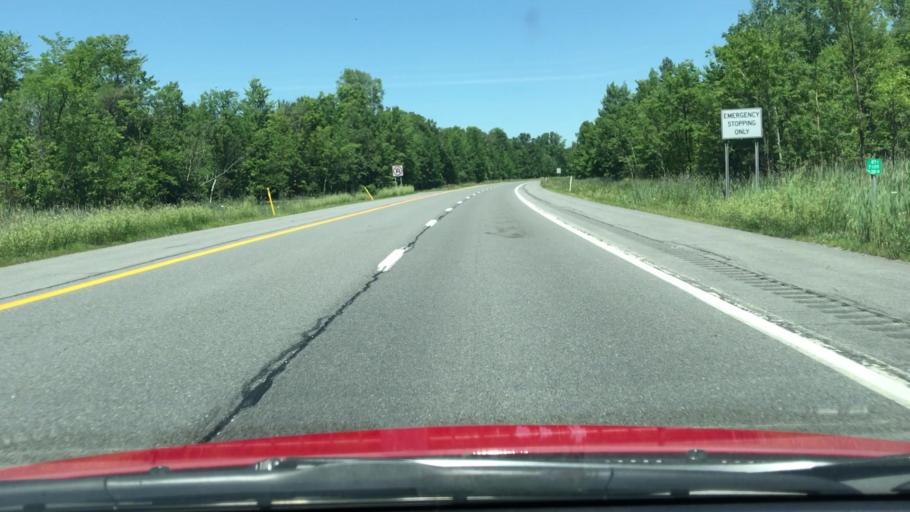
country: US
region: New York
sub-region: Clinton County
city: Champlain
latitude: 44.8980
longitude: -73.4546
